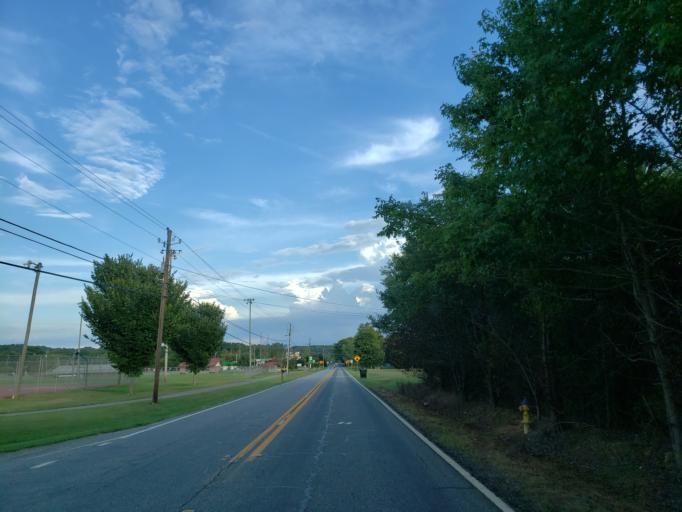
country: US
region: Georgia
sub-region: Bartow County
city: Cartersville
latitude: 34.2344
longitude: -84.8677
